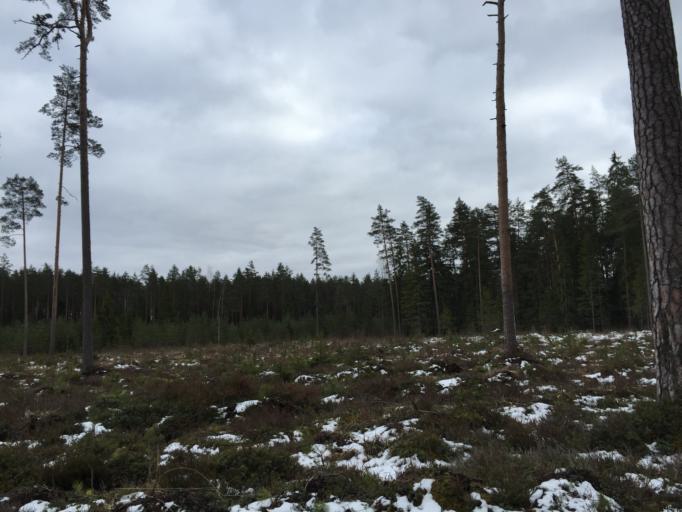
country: LV
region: Garkalne
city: Garkalne
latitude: 56.9603
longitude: 24.4784
